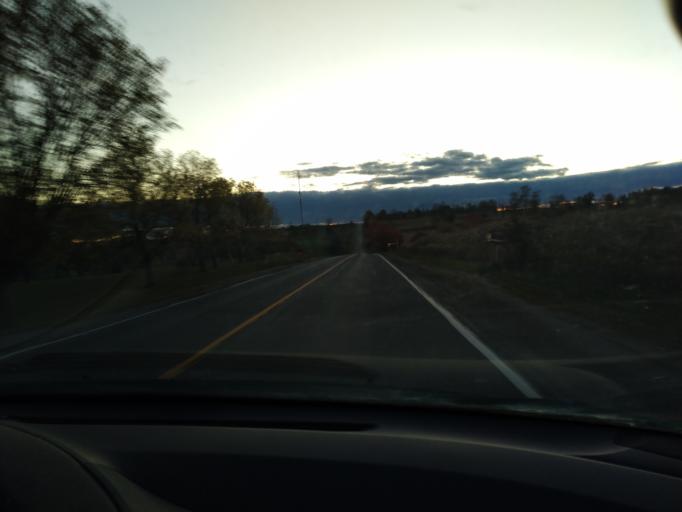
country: CA
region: Ontario
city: Innisfil
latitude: 44.2404
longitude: -79.6512
